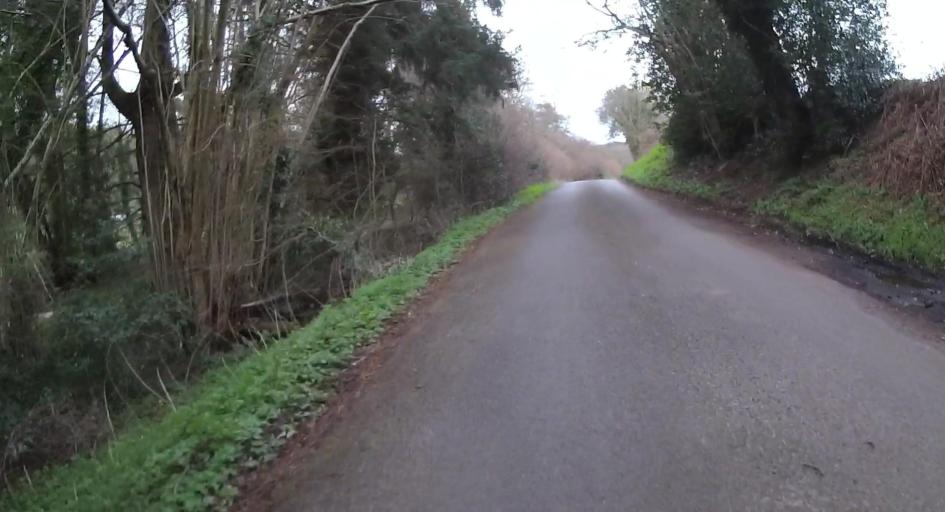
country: GB
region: England
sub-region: Hampshire
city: Lindford
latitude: 51.1418
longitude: -0.8272
